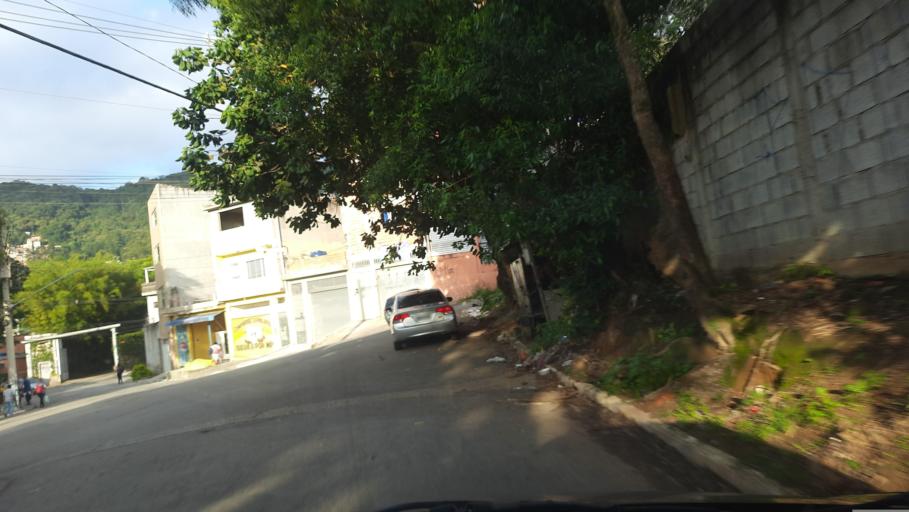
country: BR
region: Sao Paulo
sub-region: Caieiras
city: Caieiras
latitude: -23.4342
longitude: -46.7128
